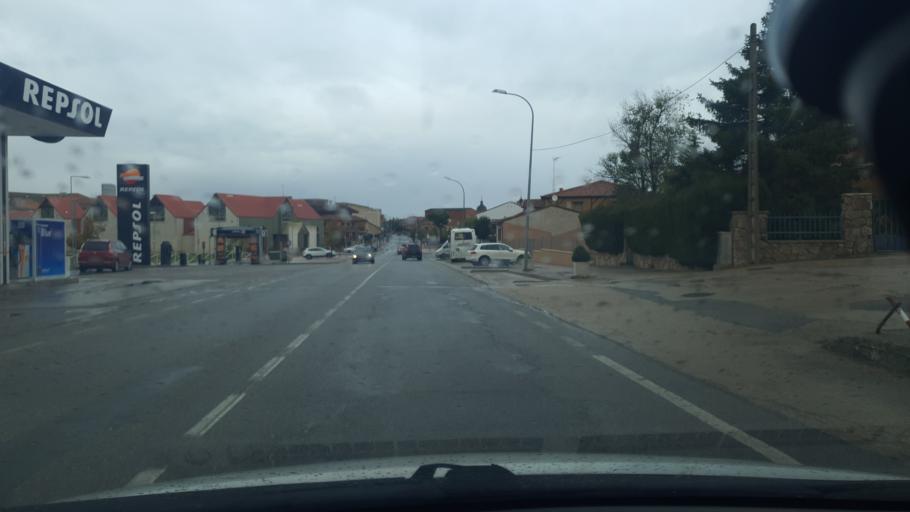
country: ES
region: Castille and Leon
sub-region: Provincia de Segovia
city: Carbonero el Mayor
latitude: 41.1173
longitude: -4.2631
